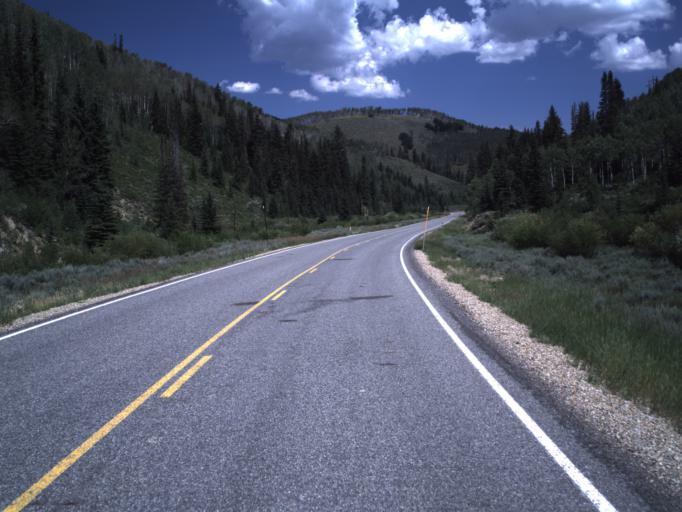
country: US
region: Utah
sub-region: Sanpete County
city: Fairview
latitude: 39.6567
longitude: -111.1548
